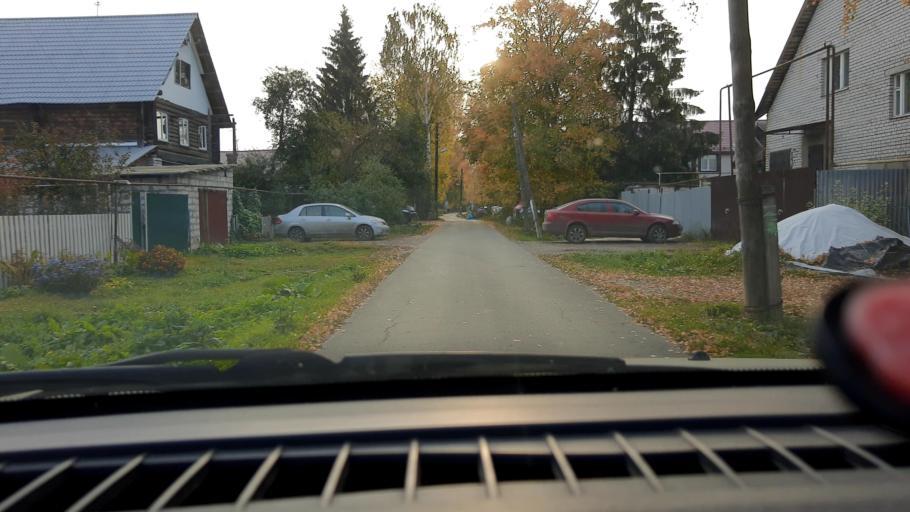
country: RU
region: Nizjnij Novgorod
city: Gorbatovka
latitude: 56.3653
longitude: 43.8368
